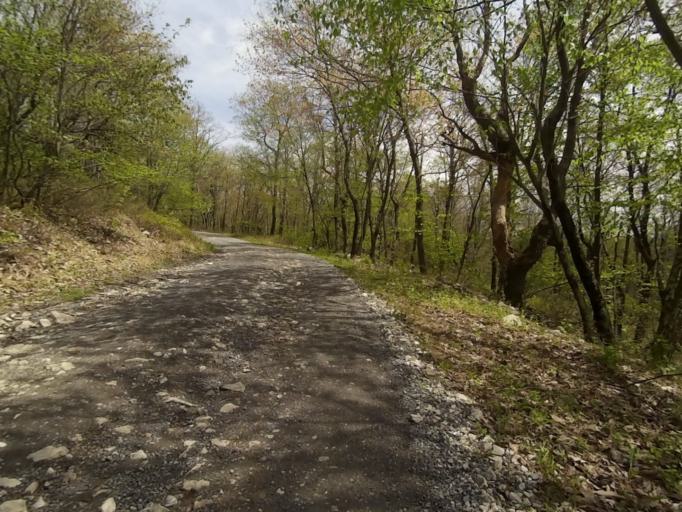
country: US
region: Pennsylvania
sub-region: Centre County
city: Boalsburg
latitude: 40.7504
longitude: -77.7683
